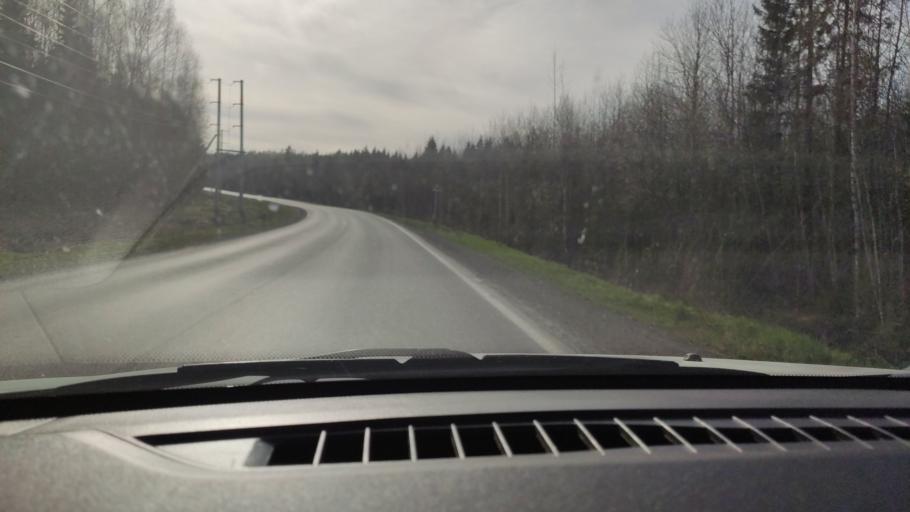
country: RU
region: Perm
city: Novyye Lyady
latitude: 57.9602
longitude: 56.5437
